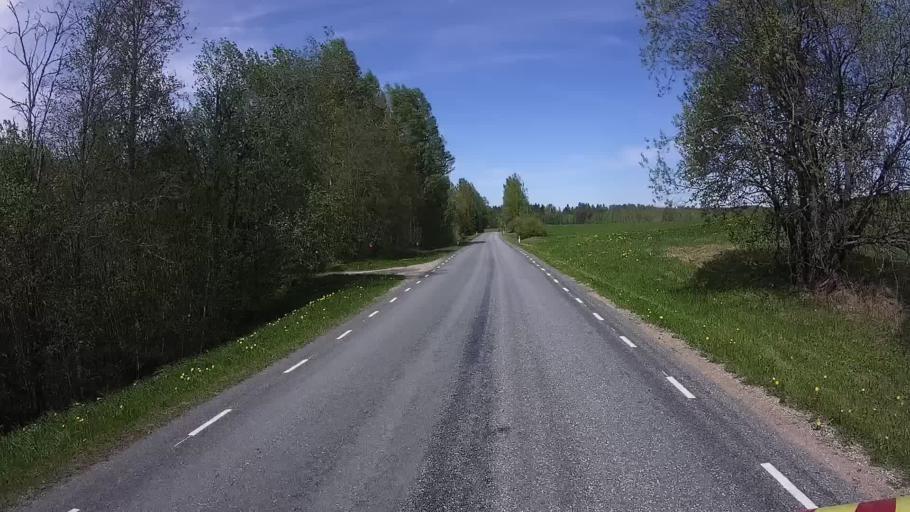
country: EE
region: Valgamaa
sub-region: Valga linn
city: Valga
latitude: 57.6596
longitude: 26.2888
